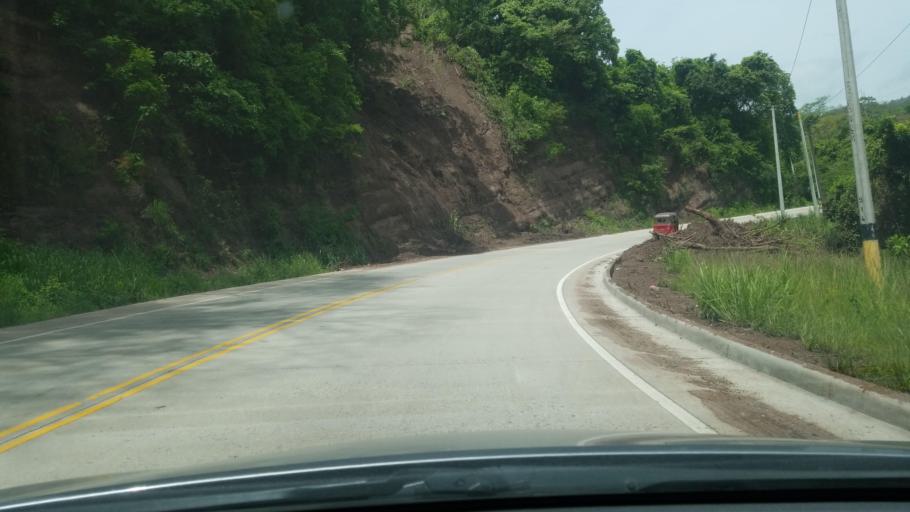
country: HN
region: Copan
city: Veracruz
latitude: 14.8800
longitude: -88.7766
